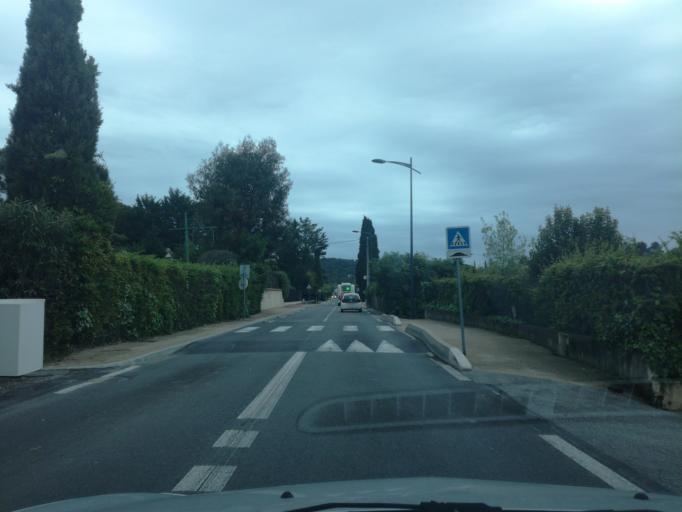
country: FR
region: Provence-Alpes-Cote d'Azur
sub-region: Departement des Alpes-Maritimes
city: Mougins
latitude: 43.6037
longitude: 7.0108
